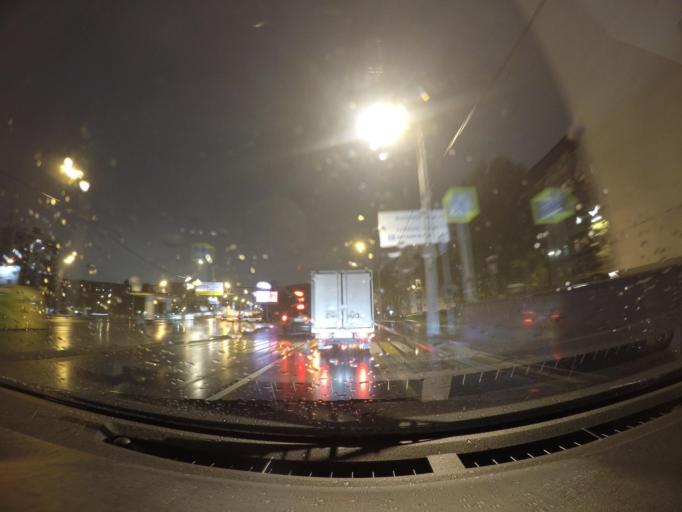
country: RU
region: Moskovskaya
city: Kozhukhovo
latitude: 55.7058
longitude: 37.6681
